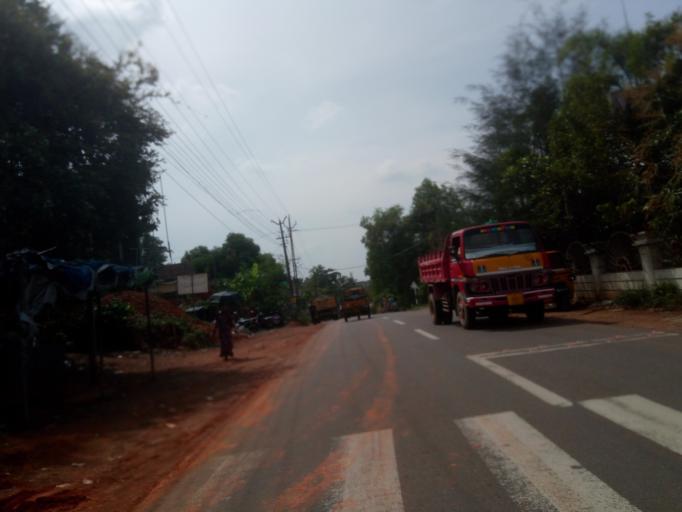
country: IN
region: Kerala
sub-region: Malappuram
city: Ponnani
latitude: 10.7741
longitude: 76.0161
